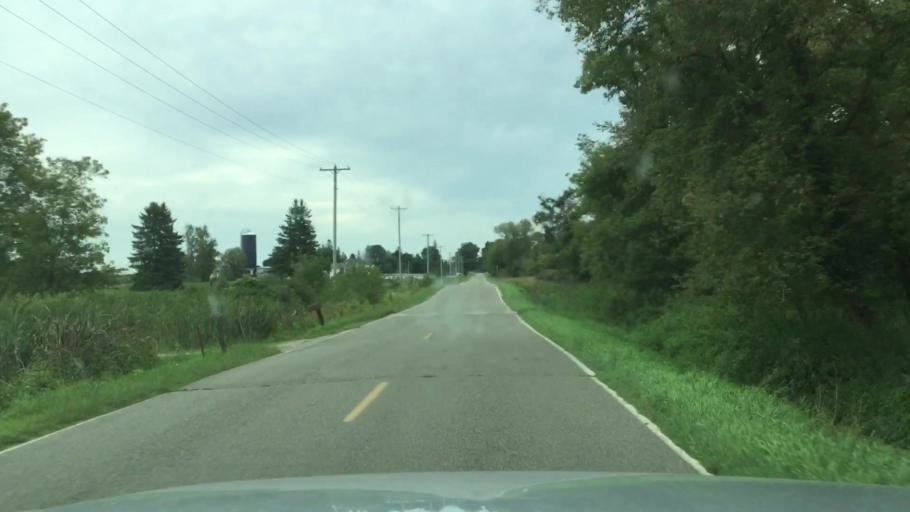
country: US
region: Michigan
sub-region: Shiawassee County
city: Durand
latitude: 42.8230
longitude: -83.9935
